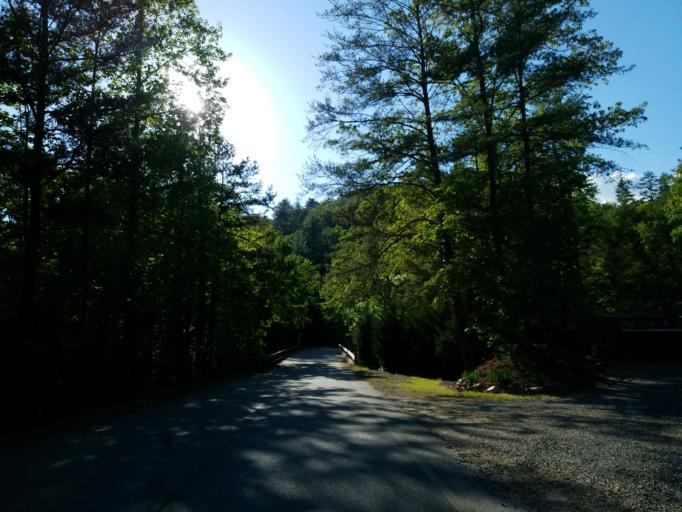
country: US
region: Georgia
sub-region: Fannin County
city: Blue Ridge
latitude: 34.7458
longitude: -84.1511
